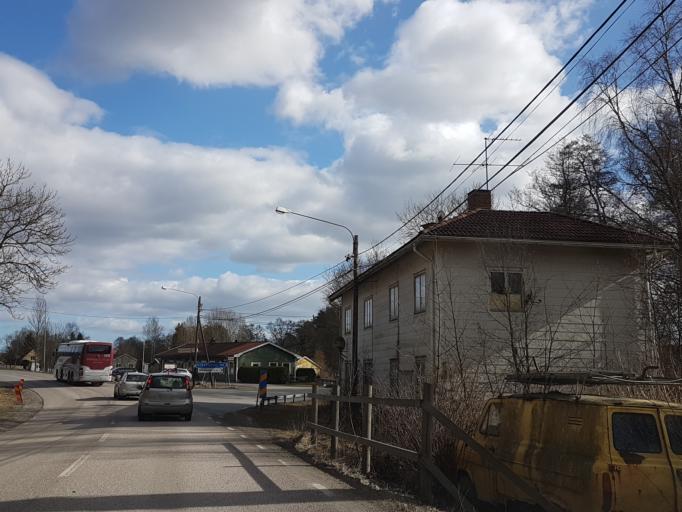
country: SE
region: Stockholm
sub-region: Norrtalje Kommun
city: Rimbo
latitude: 59.7370
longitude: 18.4929
